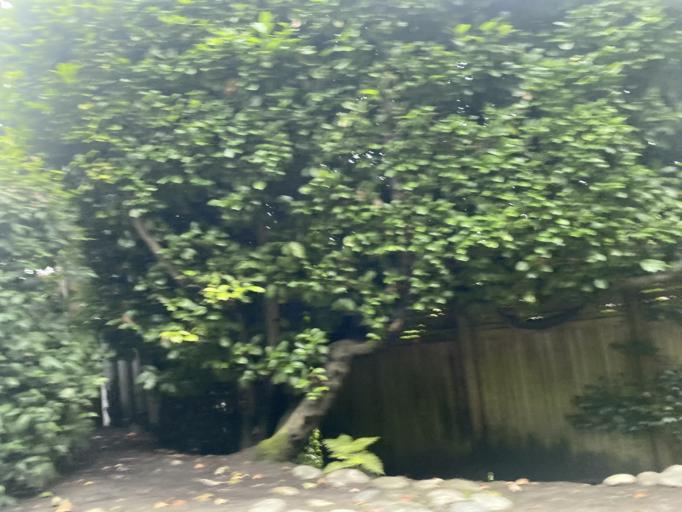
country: US
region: Washington
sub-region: King County
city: Seattle
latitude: 47.6399
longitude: -122.4129
